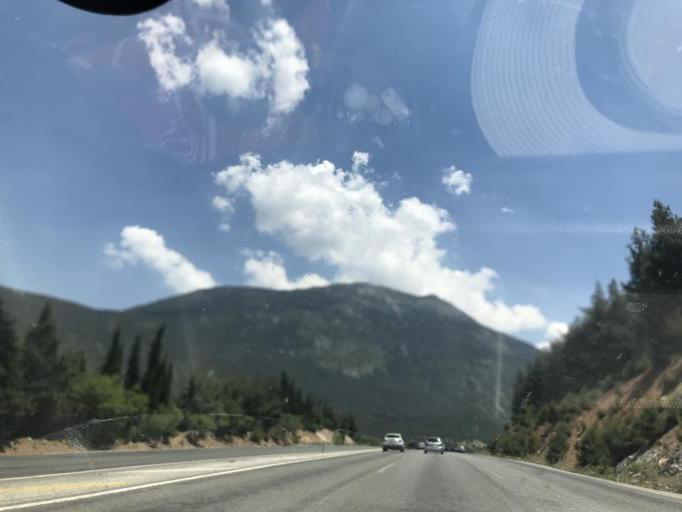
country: TR
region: Denizli
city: Honaz
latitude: 37.7258
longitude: 29.2037
